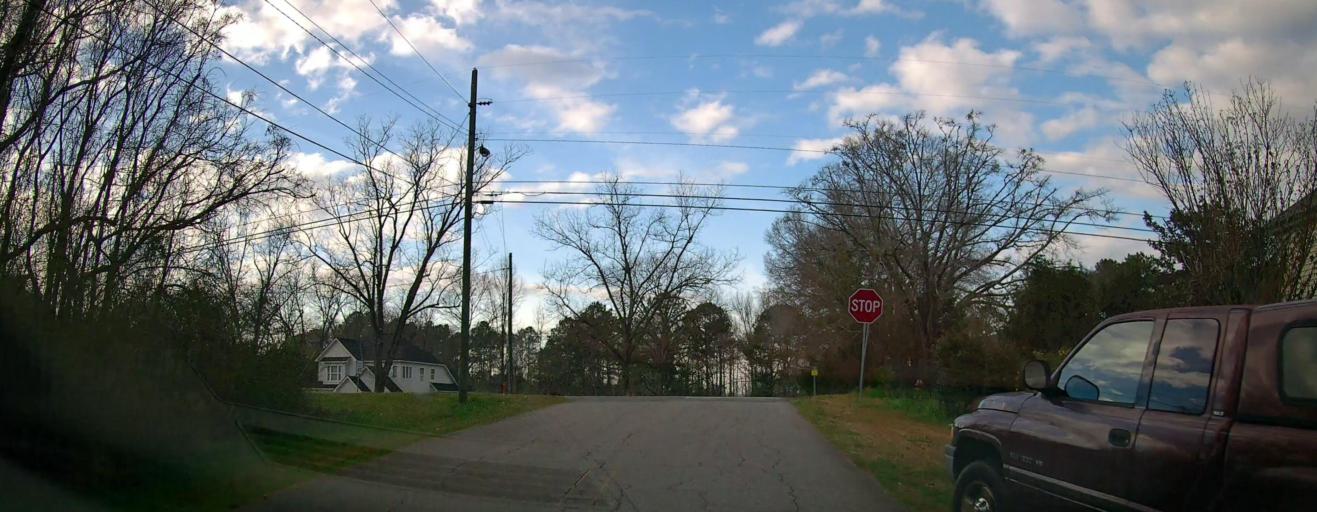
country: US
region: Georgia
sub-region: Harris County
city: Hamilton
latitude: 32.6826
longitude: -84.7454
